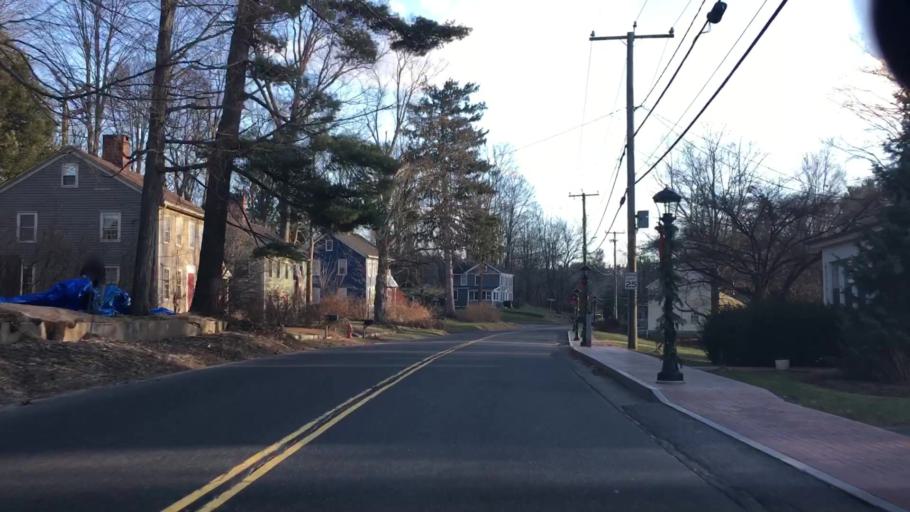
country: US
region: Connecticut
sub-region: Fairfield County
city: Newtown
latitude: 41.4194
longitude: -73.2812
